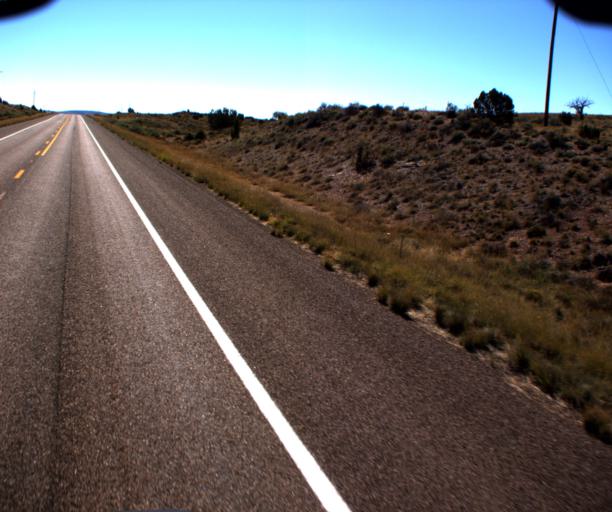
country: US
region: Arizona
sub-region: Apache County
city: Saint Johns
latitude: 34.6281
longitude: -109.6743
